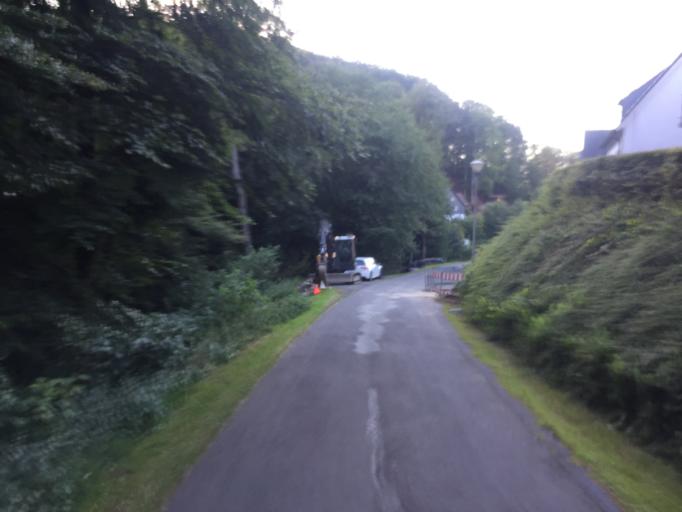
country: DE
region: North Rhine-Westphalia
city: Meinerzhagen
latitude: 51.1219
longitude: 7.6459
